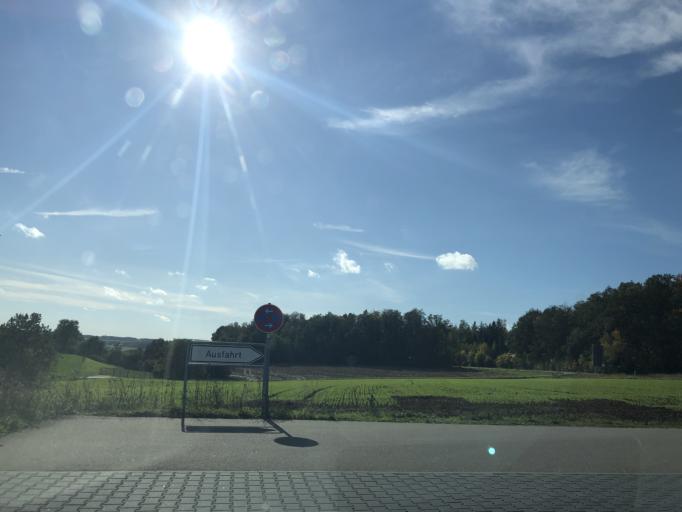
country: DE
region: Bavaria
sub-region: Upper Palatinate
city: Brunn
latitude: 49.0885
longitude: 11.8850
